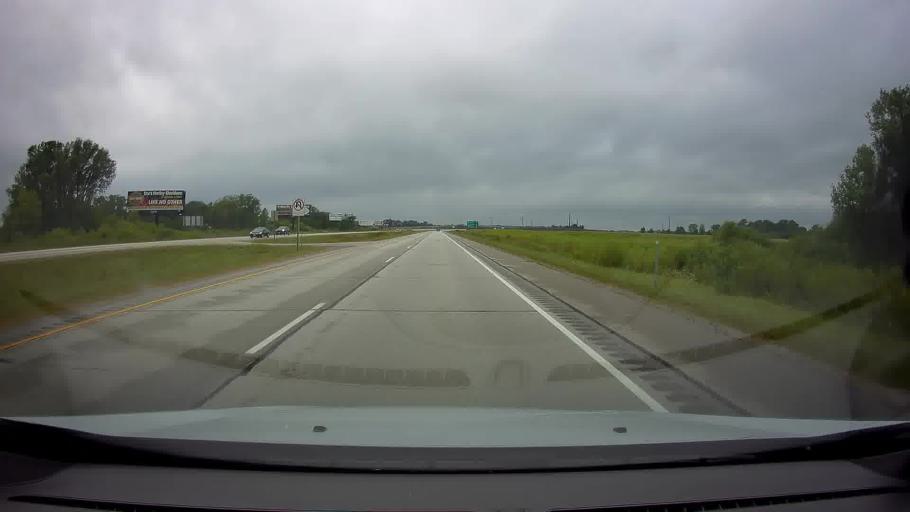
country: US
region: Wisconsin
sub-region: Brown County
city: Pulaski
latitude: 44.5992
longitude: -88.2360
